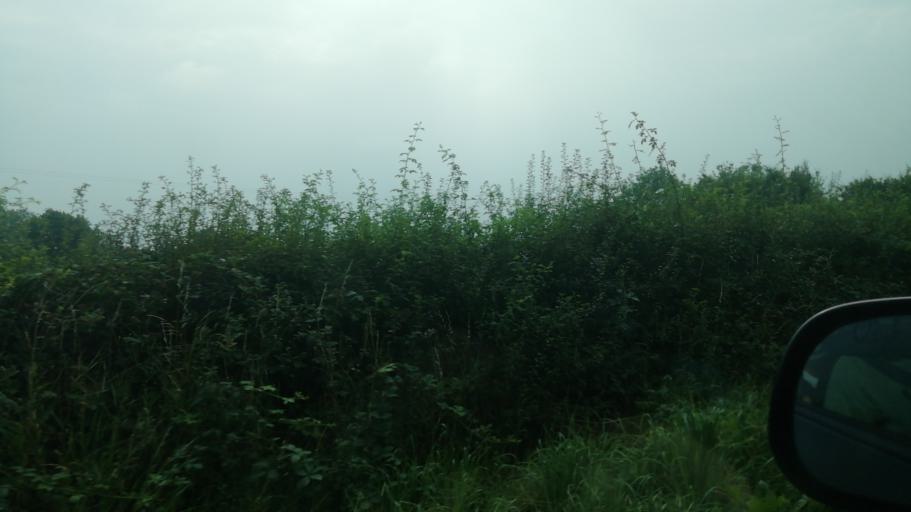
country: IE
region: Munster
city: Fethard
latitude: 52.5635
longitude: -7.5636
